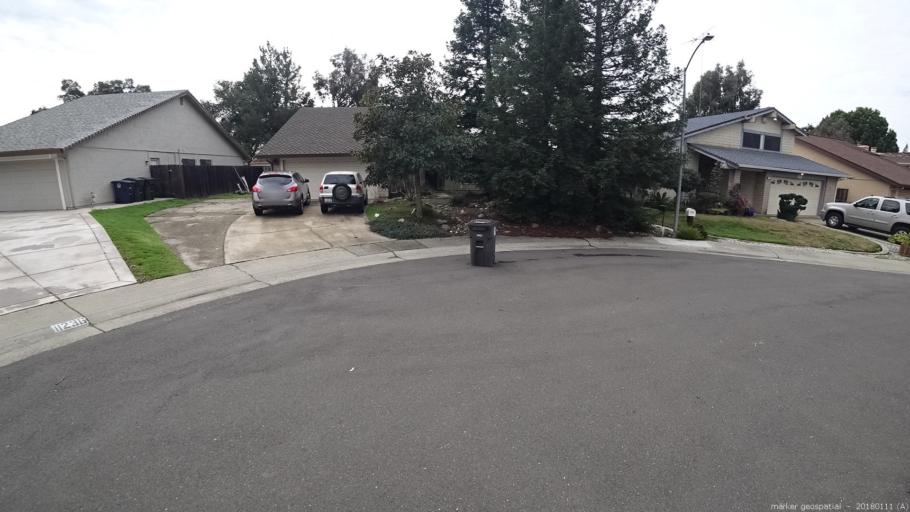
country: US
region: California
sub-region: Sacramento County
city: Fair Oaks
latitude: 38.6253
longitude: -121.2669
